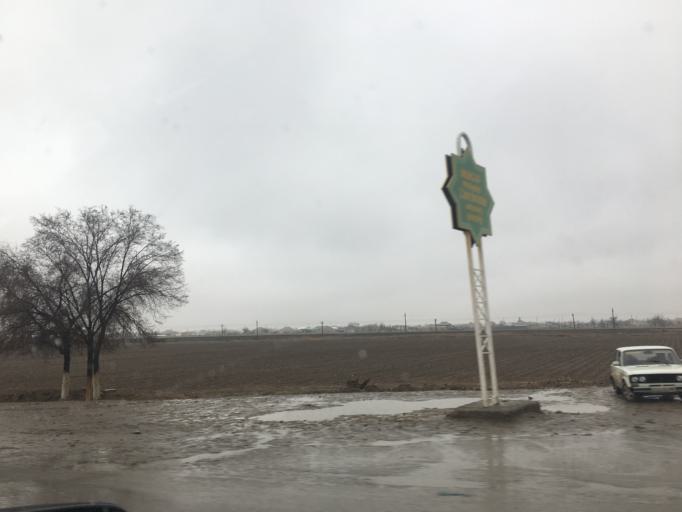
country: TM
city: Murgab
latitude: 37.5198
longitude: 61.9184
